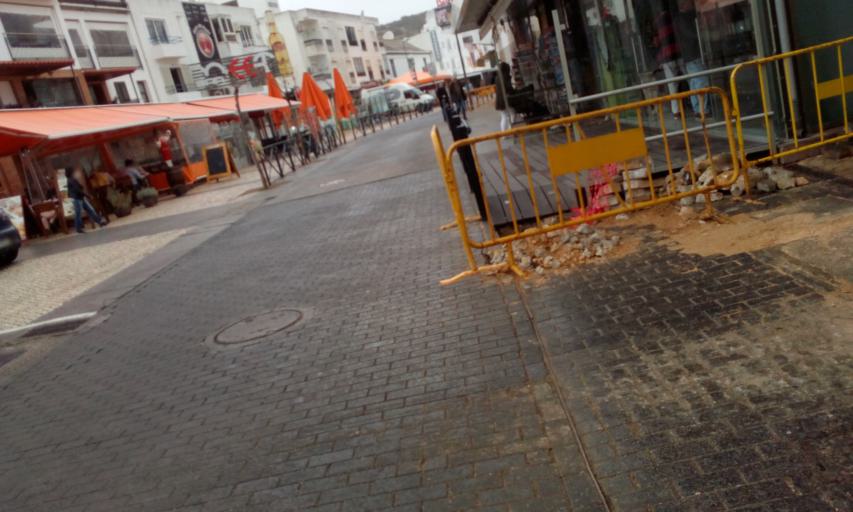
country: PT
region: Faro
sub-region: Albufeira
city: Albufeira
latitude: 37.0882
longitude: -8.2504
